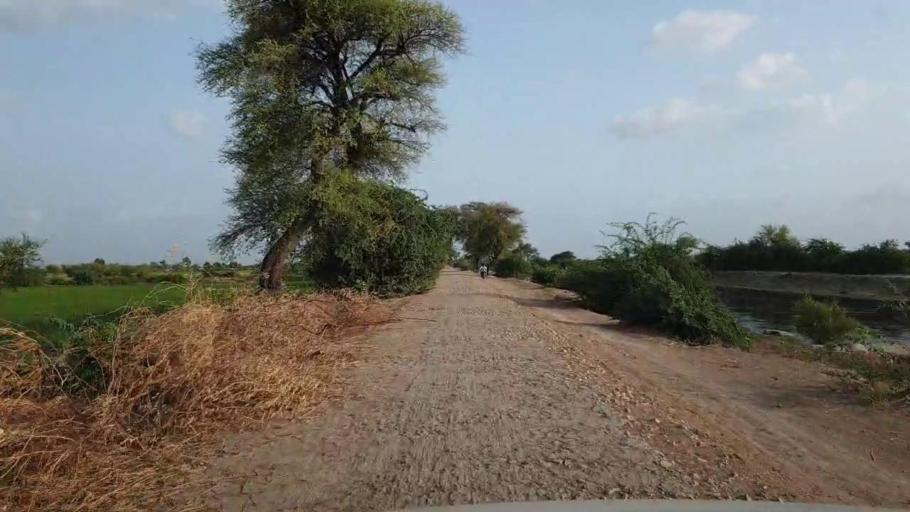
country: PK
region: Sindh
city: Kario
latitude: 24.7983
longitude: 68.6476
